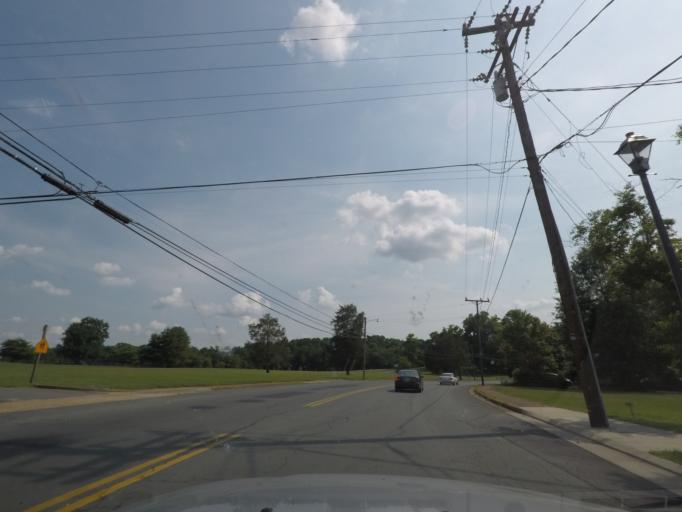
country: US
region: Virginia
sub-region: Fluvanna County
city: Weber City
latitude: 37.7616
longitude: -78.2628
